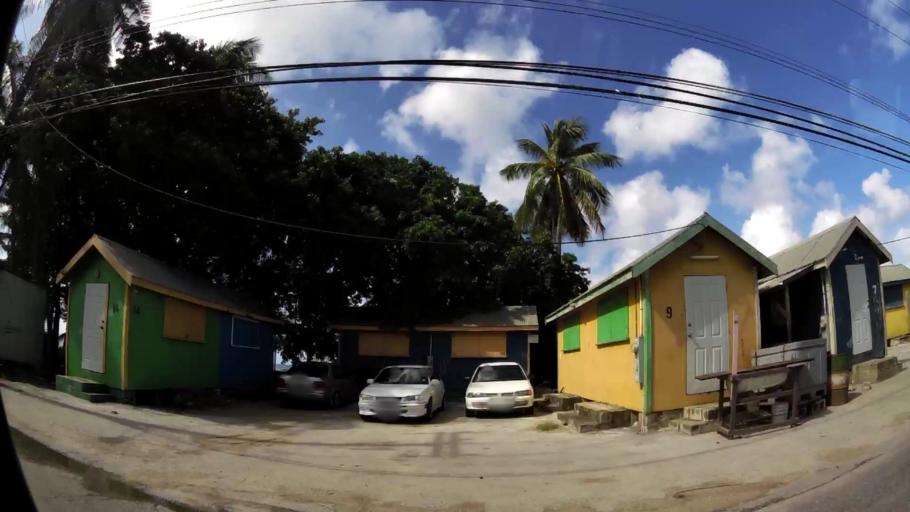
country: BB
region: Saint Peter
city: Speightstown
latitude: 13.2671
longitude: -59.6445
